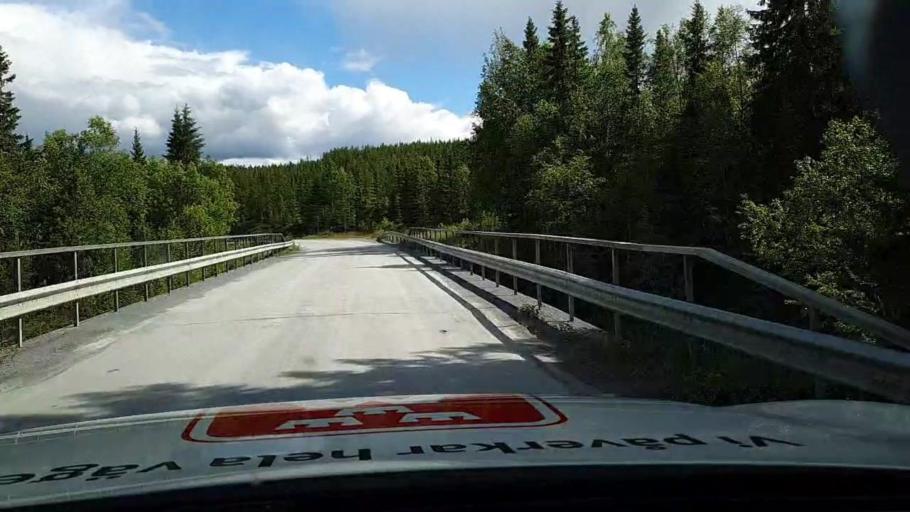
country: SE
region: Jaemtland
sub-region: Krokoms Kommun
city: Valla
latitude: 63.6634
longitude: 13.7323
